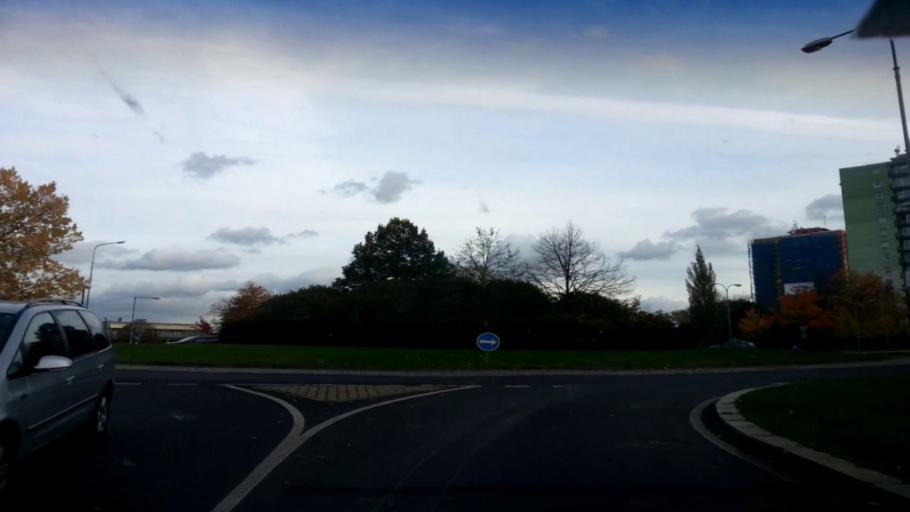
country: CZ
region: Karlovarsky
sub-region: Okres Cheb
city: Cheb
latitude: 50.0738
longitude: 12.3776
